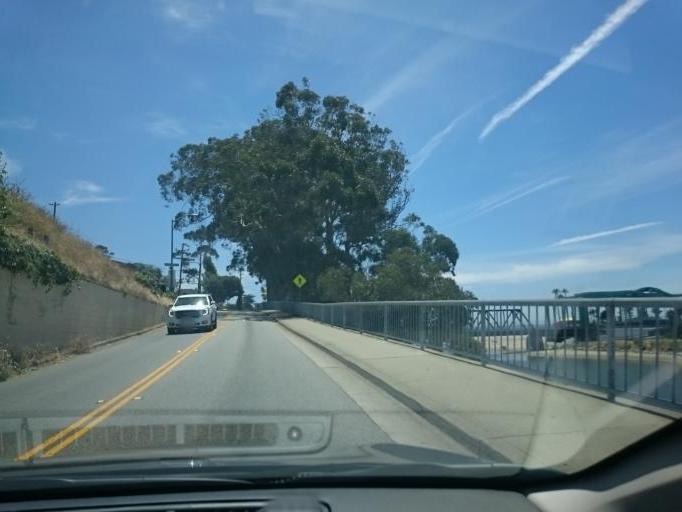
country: US
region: California
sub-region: Santa Cruz County
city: Twin Lakes
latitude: 36.9675
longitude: -122.0132
